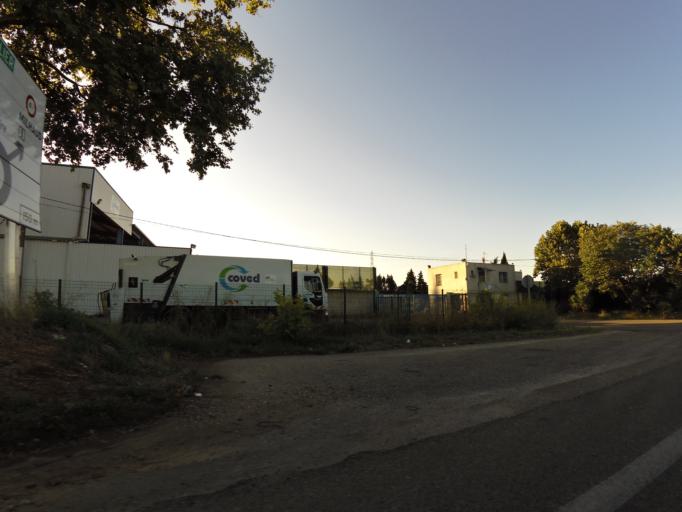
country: FR
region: Languedoc-Roussillon
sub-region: Departement du Gard
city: Milhaud
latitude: 43.8012
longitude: 4.3180
